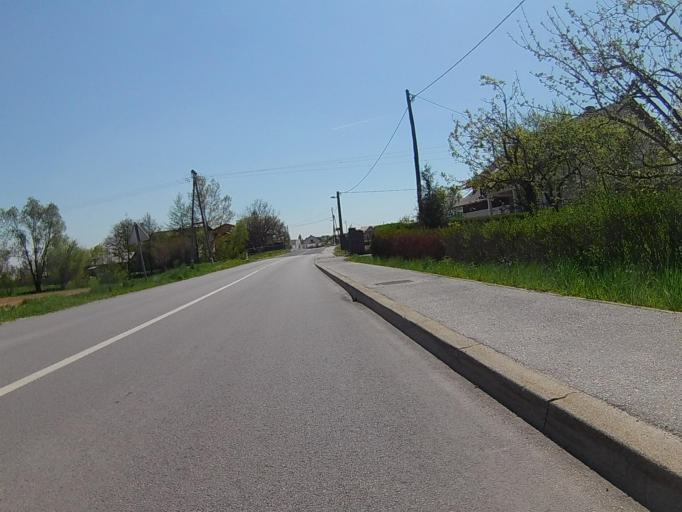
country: SI
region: Maribor
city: Razvanje
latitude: 46.5059
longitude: 15.6417
